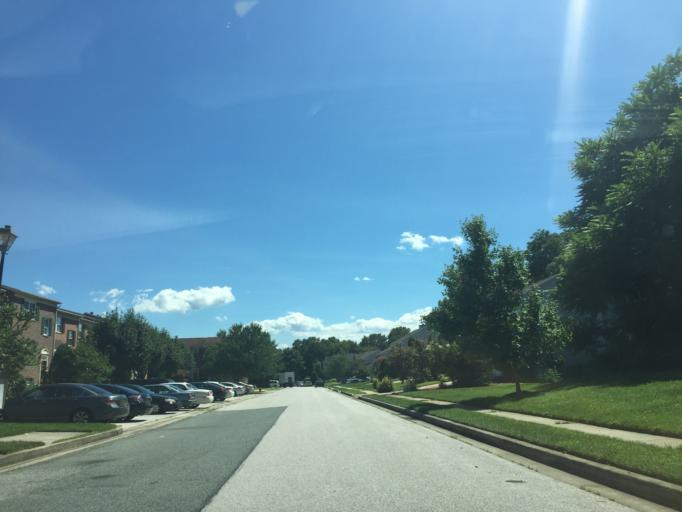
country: US
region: Maryland
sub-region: Baltimore County
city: Carney
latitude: 39.4015
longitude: -76.4968
